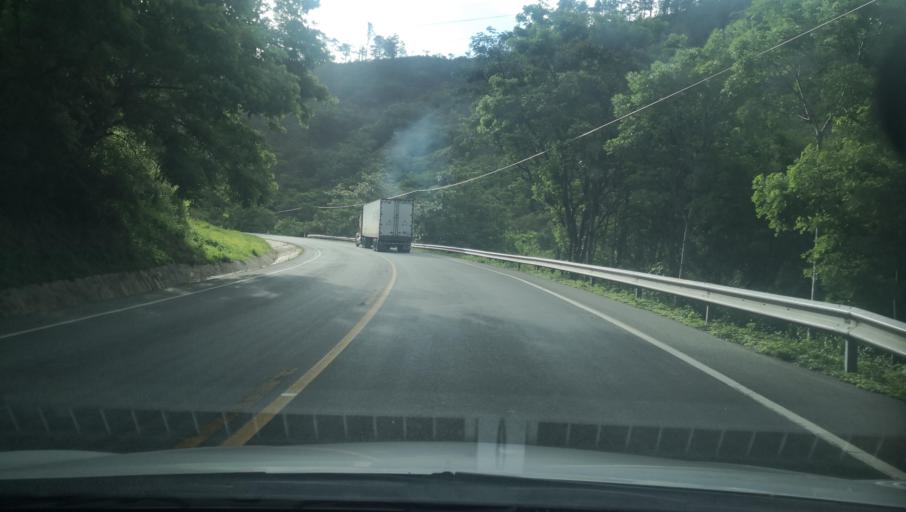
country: NI
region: Nueva Segovia
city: Mozonte
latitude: 13.7108
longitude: -86.5002
